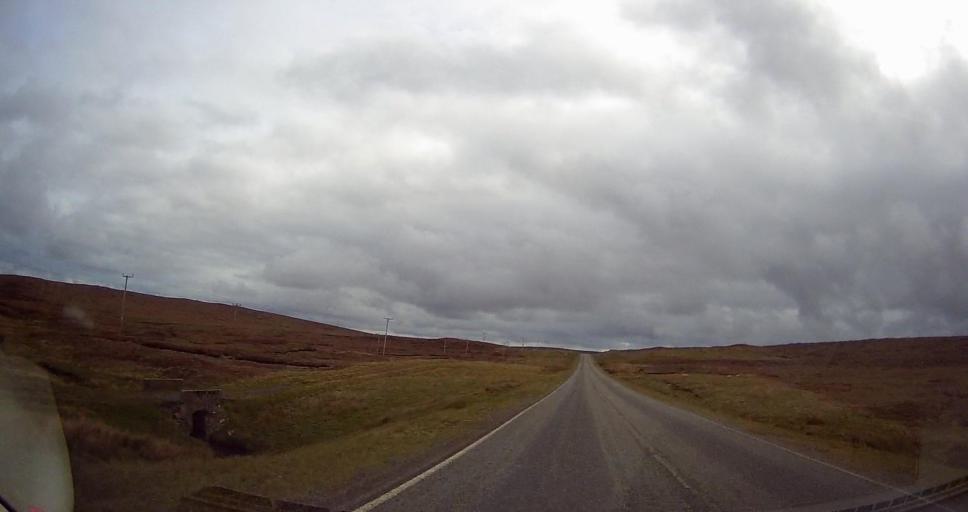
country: GB
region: Scotland
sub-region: Shetland Islands
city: Shetland
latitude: 60.5967
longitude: -1.1444
